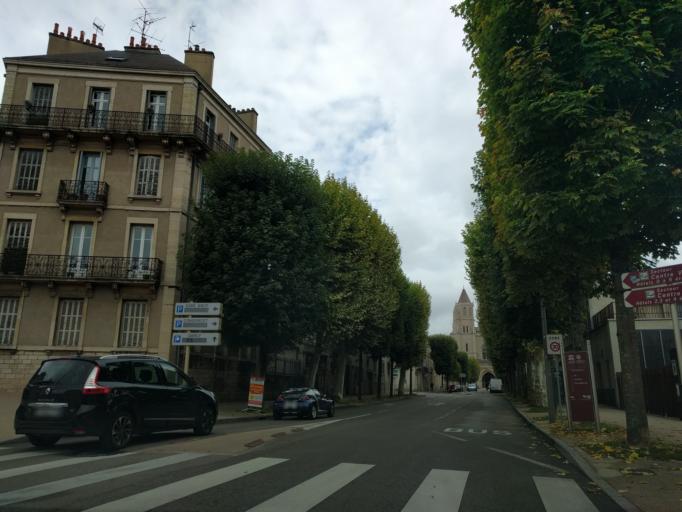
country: FR
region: Bourgogne
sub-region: Departement de la Cote-d'Or
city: Dijon
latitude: 47.3223
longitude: 5.0302
